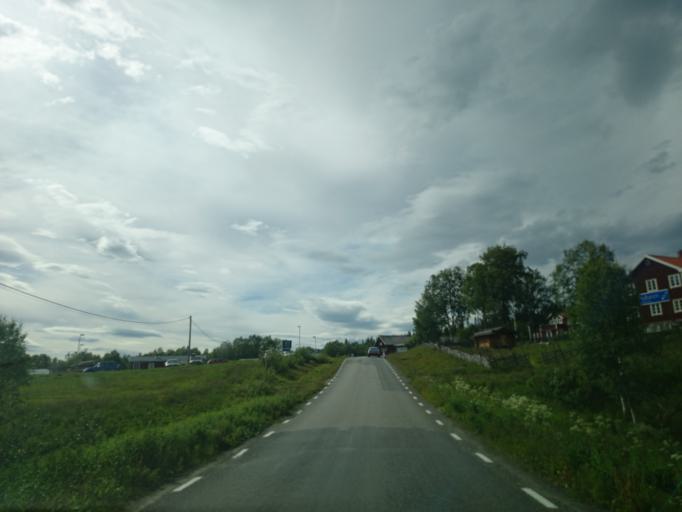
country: SE
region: Jaemtland
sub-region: Are Kommun
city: Are
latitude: 63.1477
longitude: 12.9657
